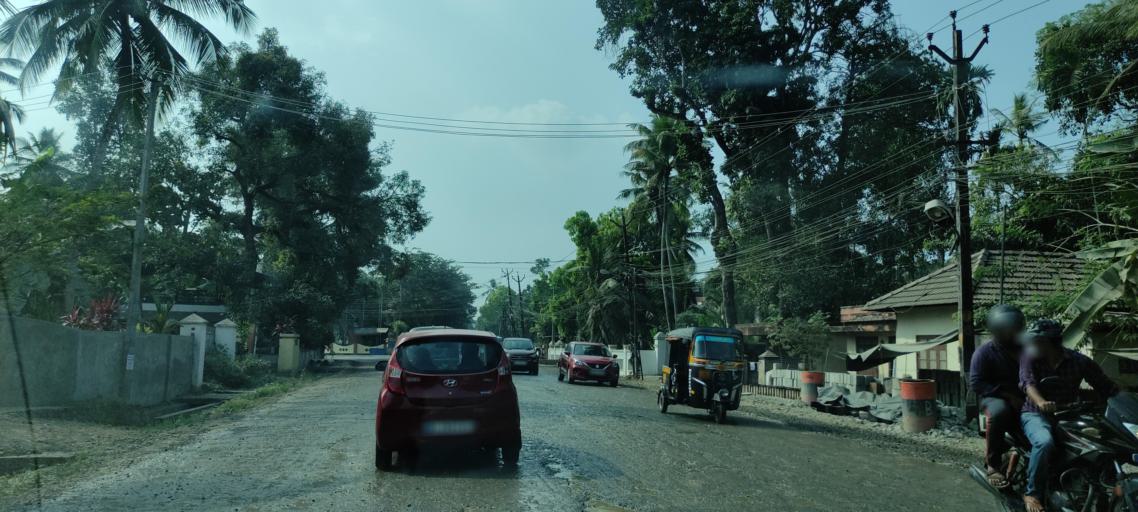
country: IN
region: Kerala
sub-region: Pattanamtitta
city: Tiruvalla
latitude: 9.3796
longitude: 76.5617
